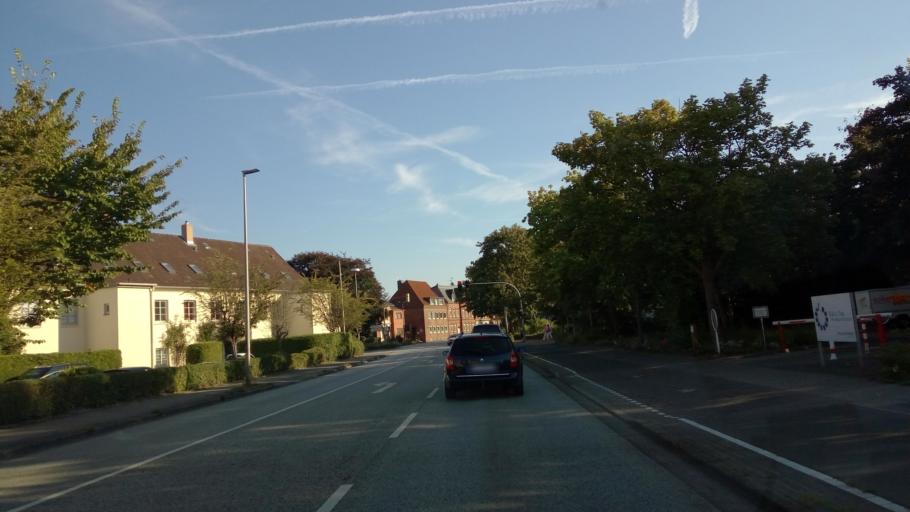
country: DE
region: Schleswig-Holstein
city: Eckernforde
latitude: 54.4667
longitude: 9.8367
